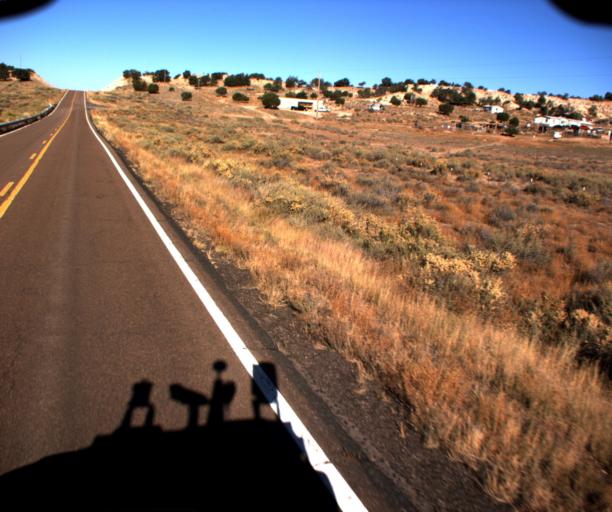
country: US
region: Arizona
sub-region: Navajo County
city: First Mesa
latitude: 35.7618
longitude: -109.9717
